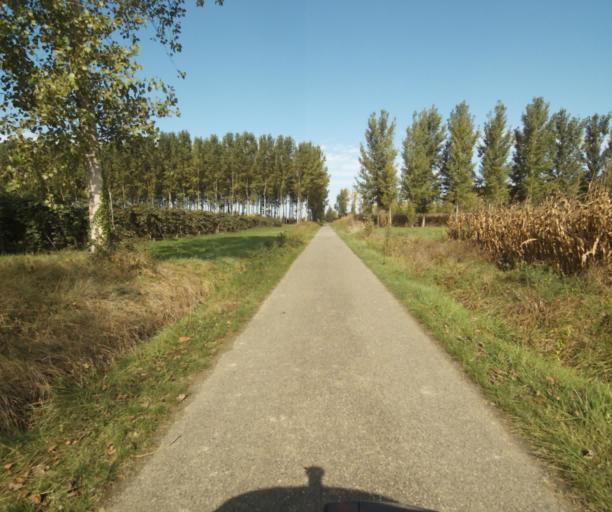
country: FR
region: Midi-Pyrenees
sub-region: Departement du Tarn-et-Garonne
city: Finhan
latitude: 43.9065
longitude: 1.2160
